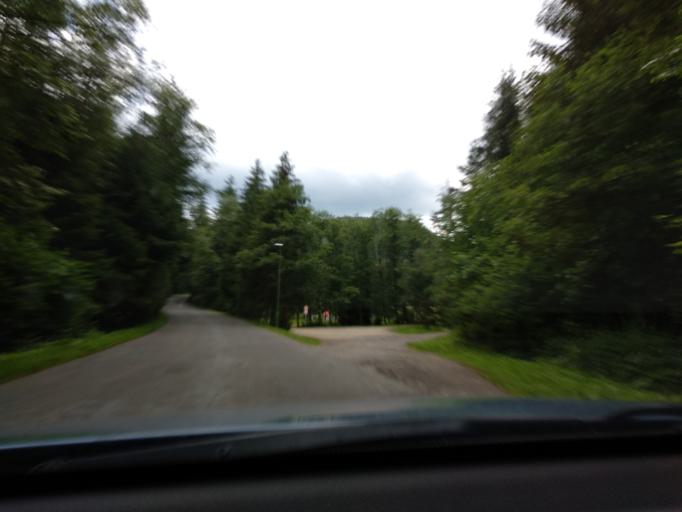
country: SK
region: Zilinsky
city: Ruzomberok
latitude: 49.0749
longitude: 19.2756
